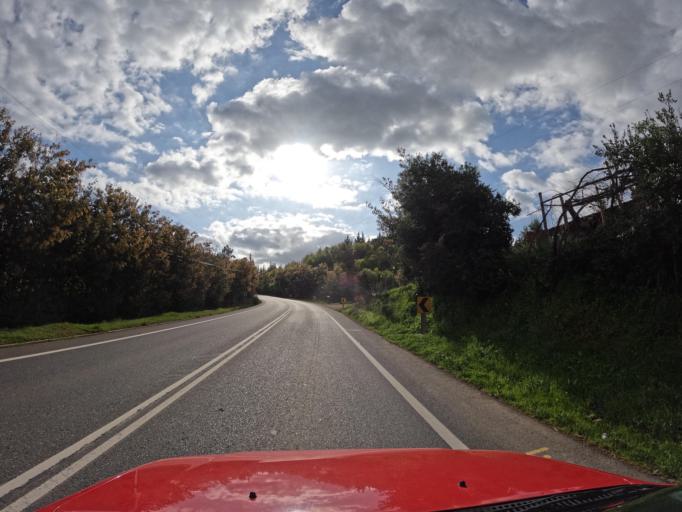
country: CL
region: Maule
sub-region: Provincia de Talca
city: Constitucion
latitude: -35.5508
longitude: -72.1438
